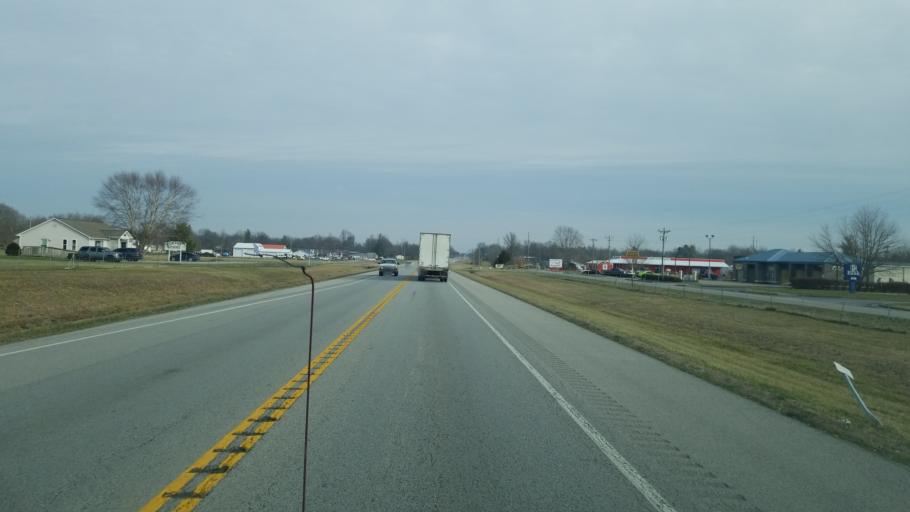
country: US
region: Kentucky
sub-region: Boyle County
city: Junction City
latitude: 37.5763
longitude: -84.7914
